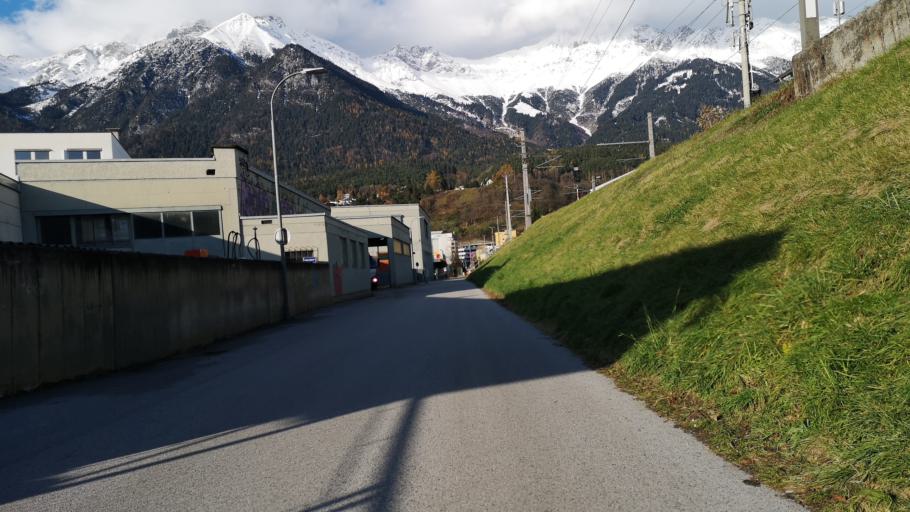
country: AT
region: Tyrol
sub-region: Innsbruck Stadt
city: Innsbruck
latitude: 47.2609
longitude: 11.3737
